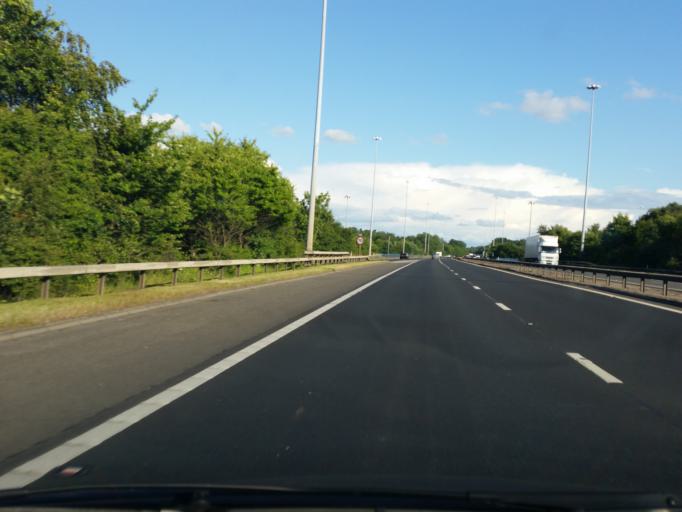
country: GB
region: Scotland
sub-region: South Lanarkshire
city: Hamilton
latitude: 55.7815
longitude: -4.0225
